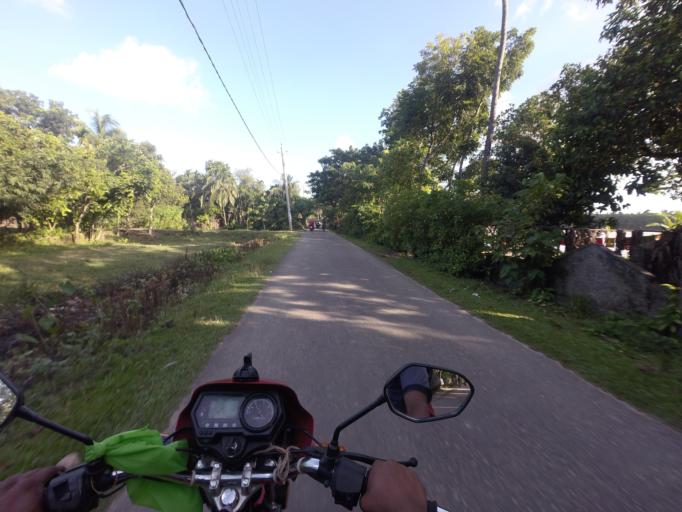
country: BD
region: Khulna
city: Khulna
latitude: 22.9065
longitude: 89.5209
